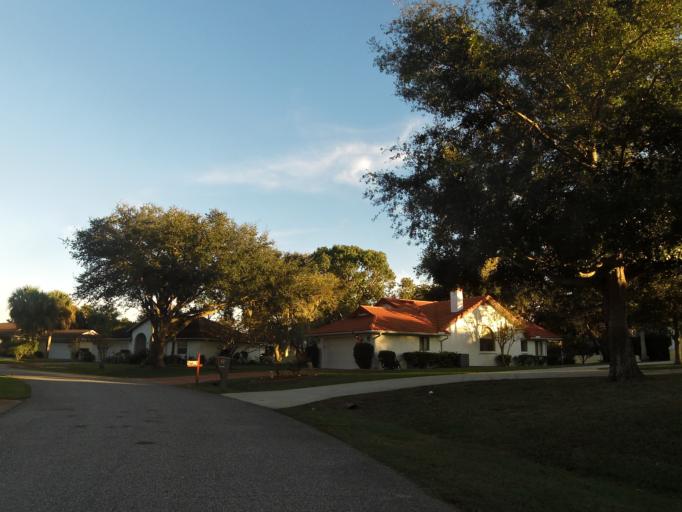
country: US
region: Florida
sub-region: Flagler County
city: Palm Coast
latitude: 29.5607
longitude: -81.2050
